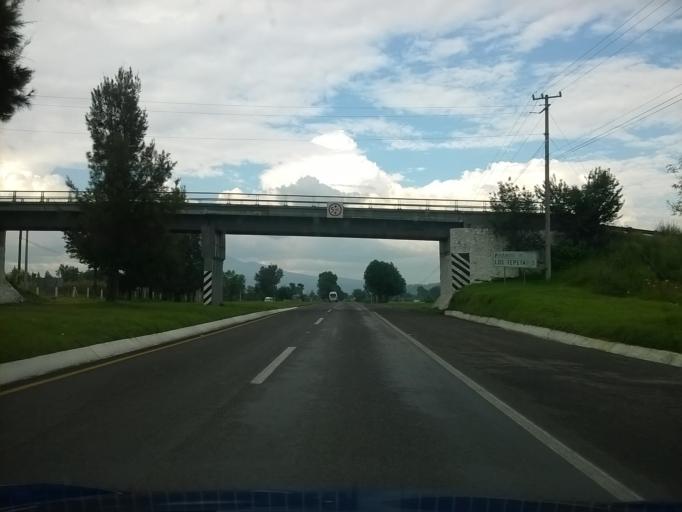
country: MX
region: Michoacan
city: Huiramba
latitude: 19.5379
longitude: -101.4655
